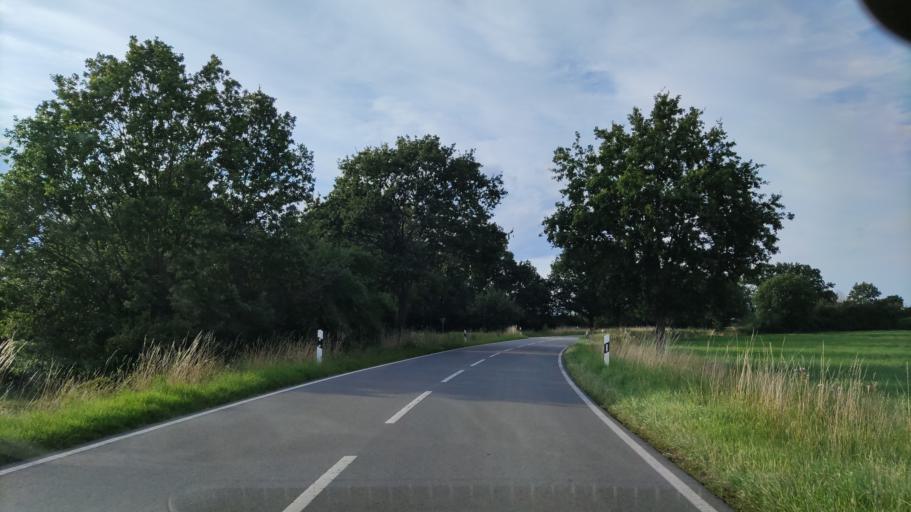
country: DE
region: Lower Saxony
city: Dannenberg
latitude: 53.1206
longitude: 11.1136
